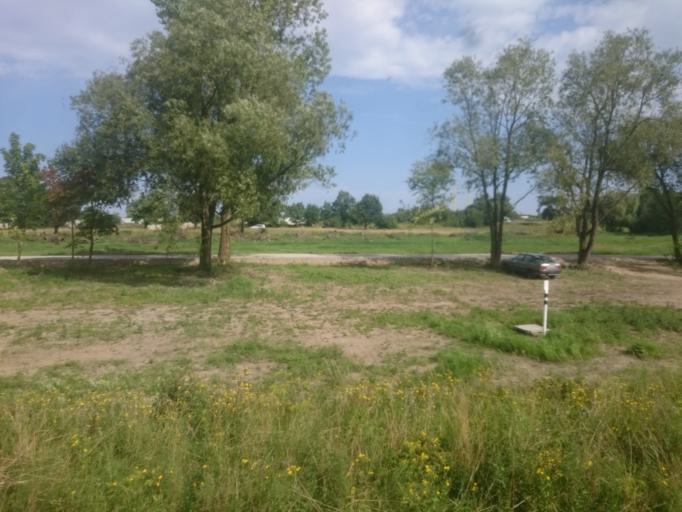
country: RU
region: Kaliningrad
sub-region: Zelenogradskiy Rayon
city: Zelenogradsk
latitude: 54.9506
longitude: 20.4473
